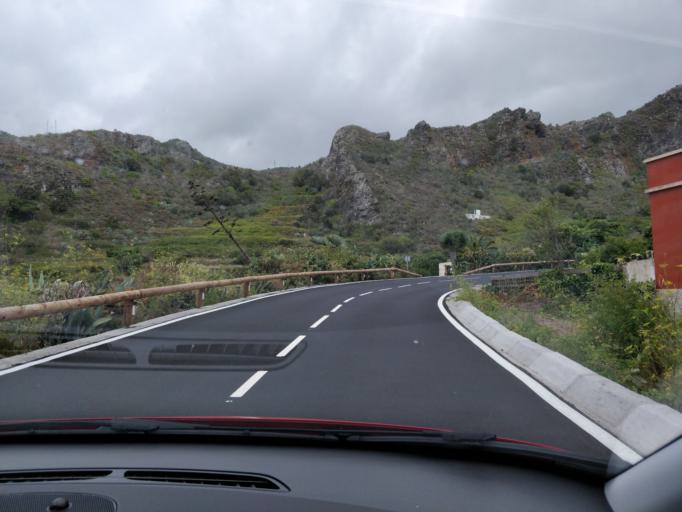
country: ES
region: Canary Islands
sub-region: Provincia de Santa Cruz de Tenerife
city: Tanque
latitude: 28.3481
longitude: -16.8440
